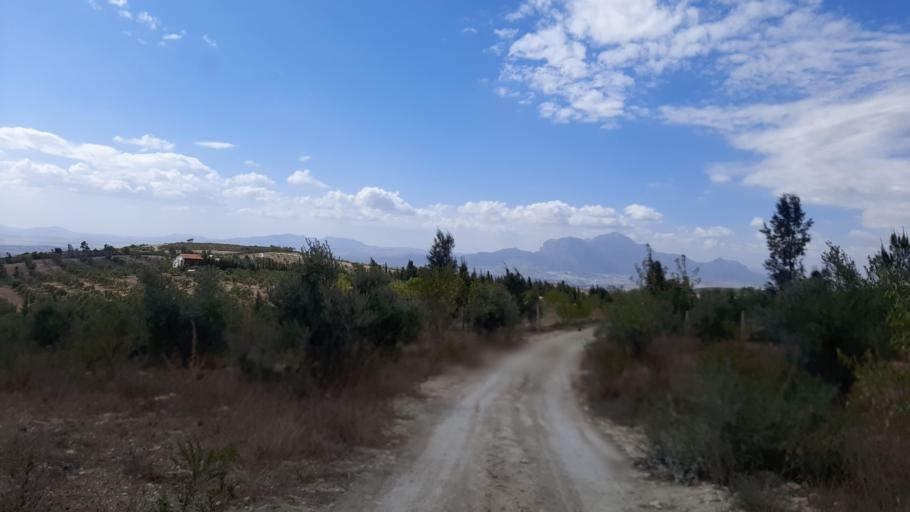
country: TN
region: Zaghwan
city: Zaghouan
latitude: 36.5033
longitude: 10.1841
